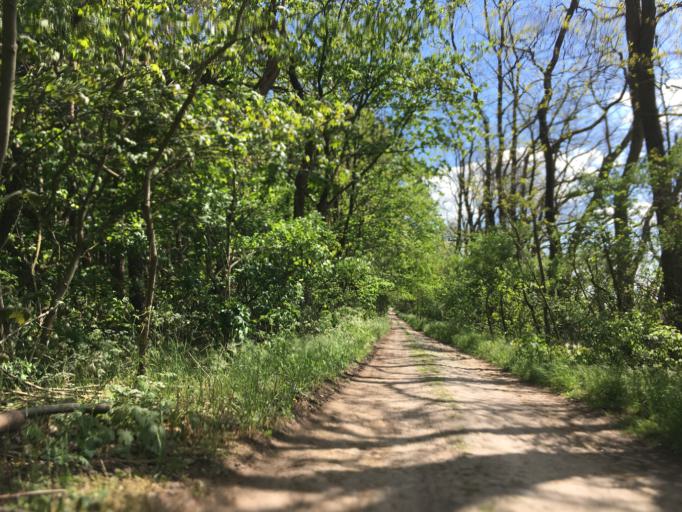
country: DE
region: Brandenburg
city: Rudnitz
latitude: 52.6721
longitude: 13.6735
